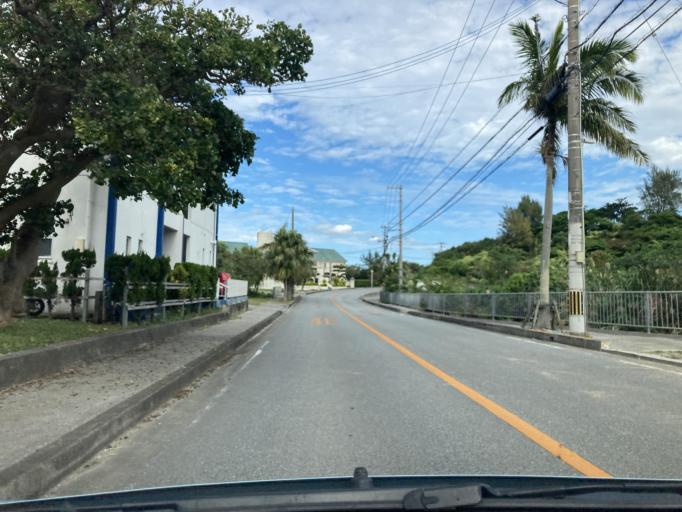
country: JP
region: Okinawa
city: Ishikawa
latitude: 26.4328
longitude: 127.7597
